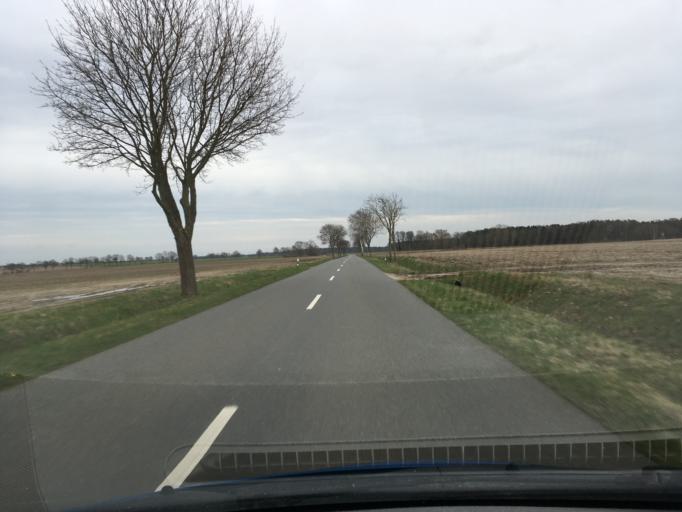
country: DE
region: Lower Saxony
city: Emmendorf
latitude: 53.0021
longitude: 10.6180
